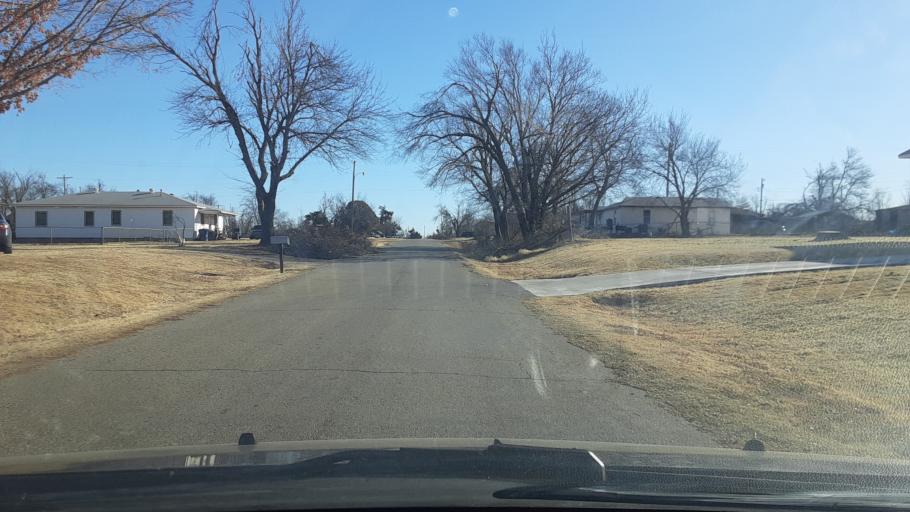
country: US
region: Oklahoma
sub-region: Logan County
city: Guthrie
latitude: 35.8729
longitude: -97.4061
